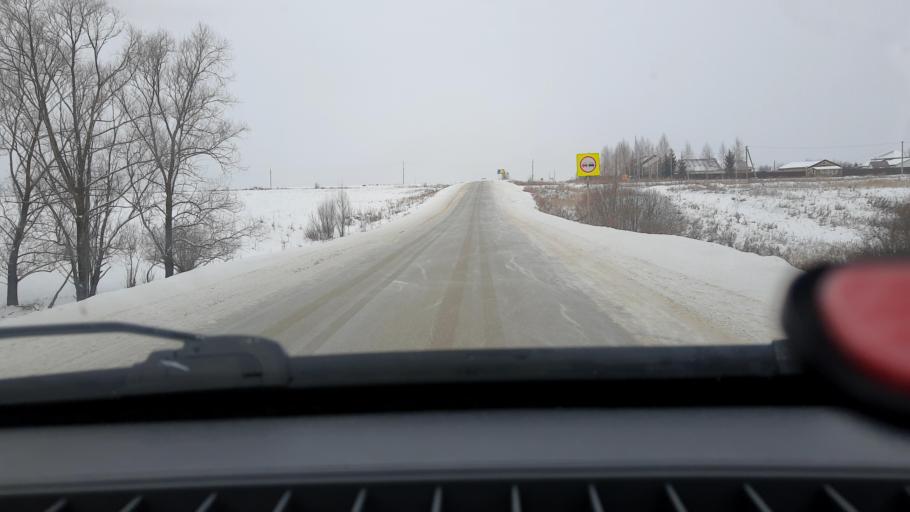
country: RU
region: Bashkortostan
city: Iglino
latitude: 54.7063
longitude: 56.4037
